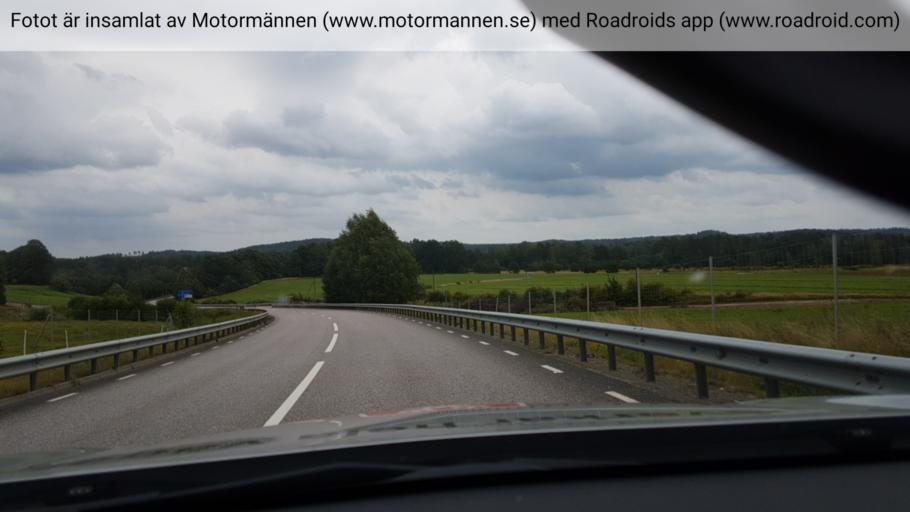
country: SE
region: Vaestra Goetaland
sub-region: Marks Kommun
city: Kinna
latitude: 57.4785
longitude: 12.6927
